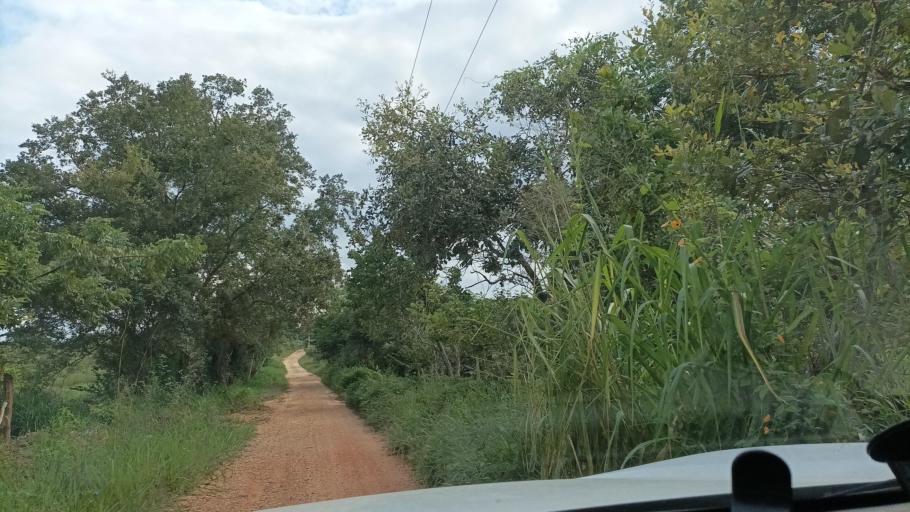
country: MX
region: Veracruz
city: Oluta
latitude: 17.9402
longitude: -94.8822
